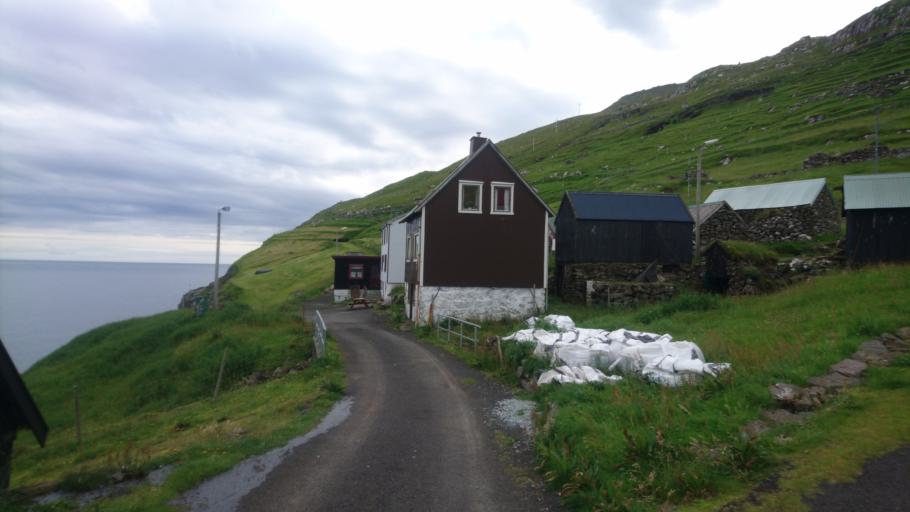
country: FO
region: Nordoyar
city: Klaksvik
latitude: 62.3290
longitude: -6.2767
